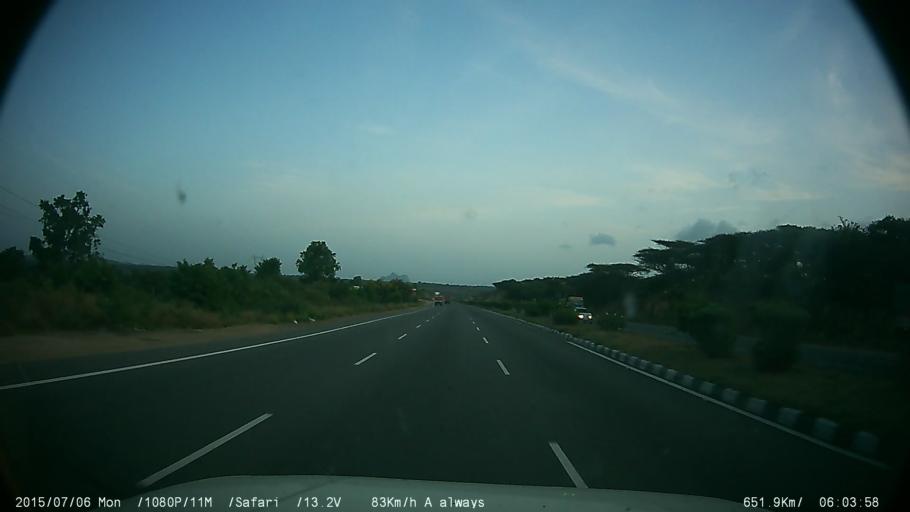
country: IN
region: Tamil Nadu
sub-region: Krishnagiri
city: Krishnagiri
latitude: 12.6105
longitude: 78.0926
